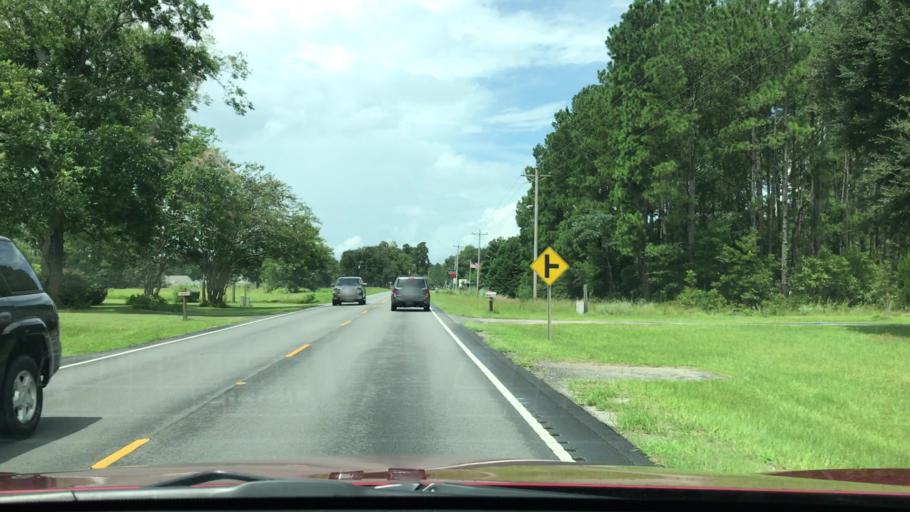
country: US
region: South Carolina
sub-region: Horry County
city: Red Hill
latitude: 33.9021
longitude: -78.8914
